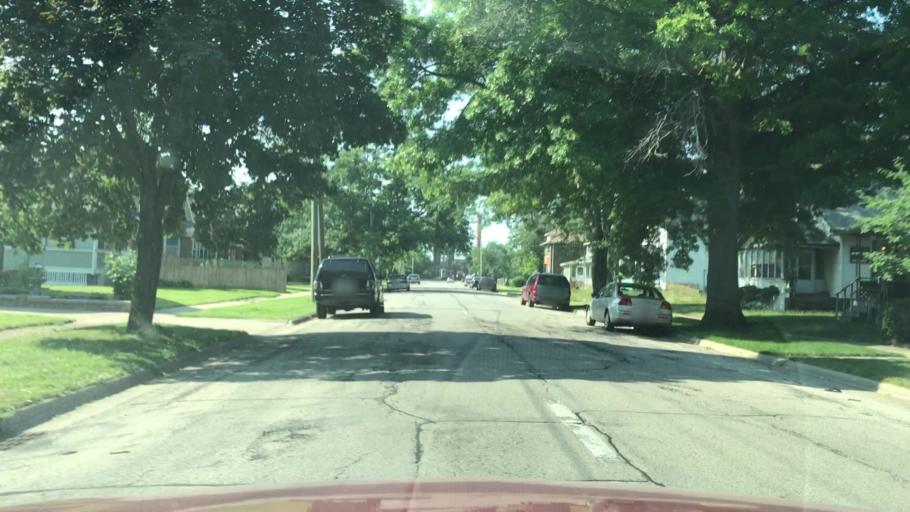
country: US
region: Illinois
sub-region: Winnebago County
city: Rockford
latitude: 42.2441
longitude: -89.0825
